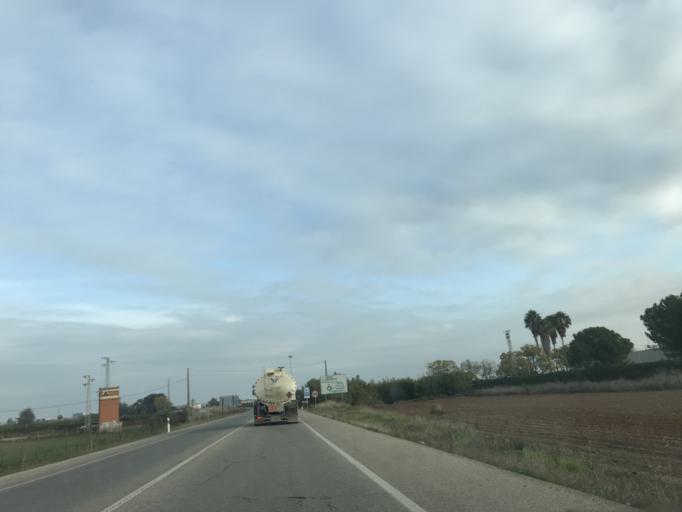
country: ES
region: Andalusia
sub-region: Provincia de Sevilla
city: La Rinconada
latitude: 37.4661
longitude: -5.9720
